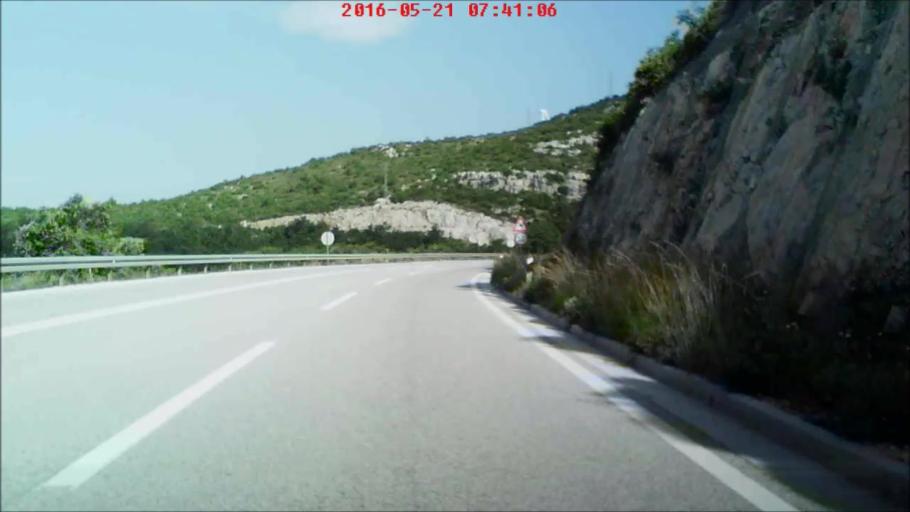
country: HR
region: Dubrovacko-Neretvanska
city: Podgora
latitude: 42.8055
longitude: 17.8186
